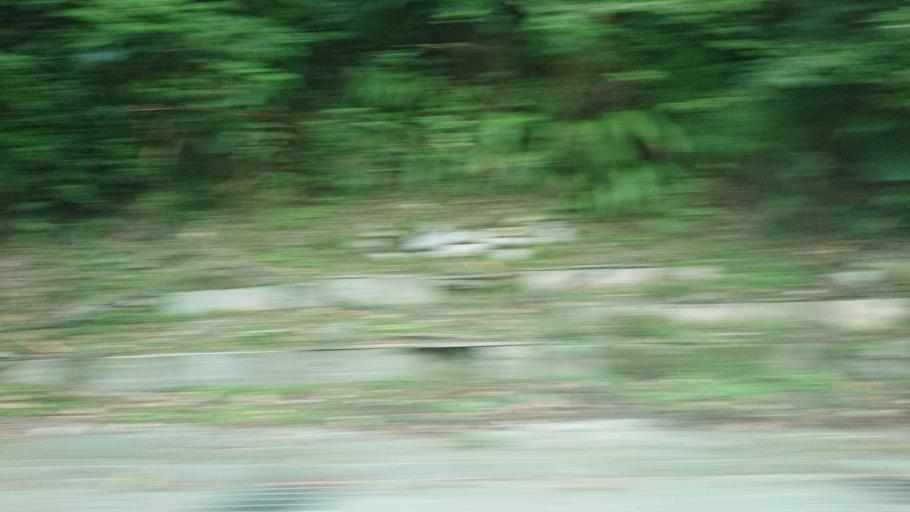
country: TW
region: Taiwan
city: Daxi
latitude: 24.8736
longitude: 121.3869
